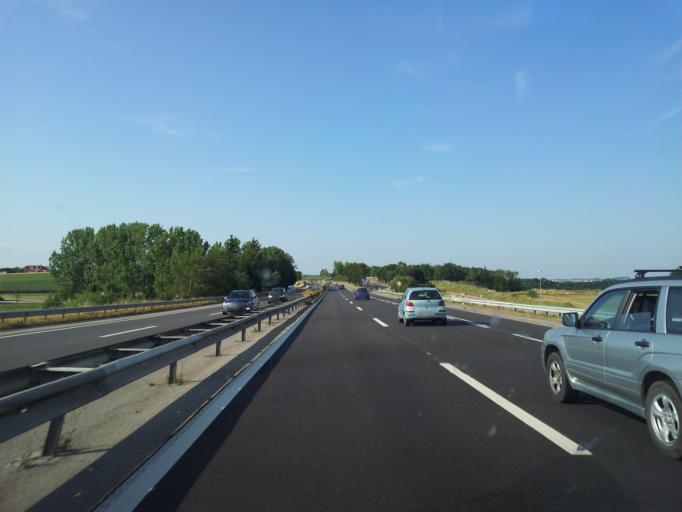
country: CH
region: Fribourg
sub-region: Sarine District
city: Matran
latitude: 46.7509
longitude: 7.0887
